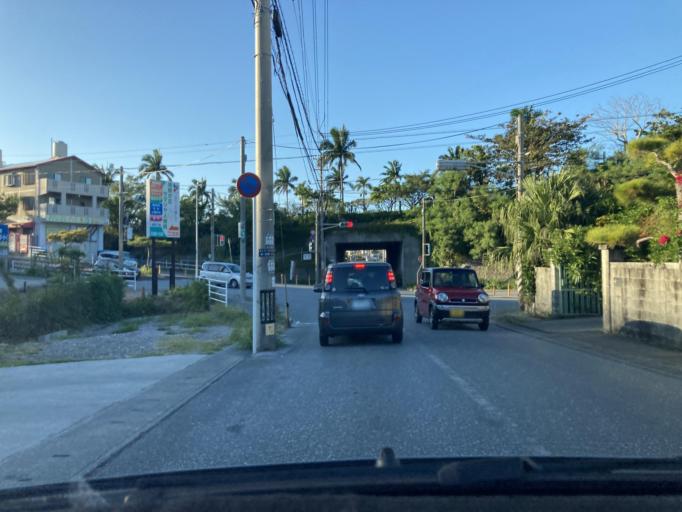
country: JP
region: Okinawa
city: Naha-shi
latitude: 26.2118
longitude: 127.7296
